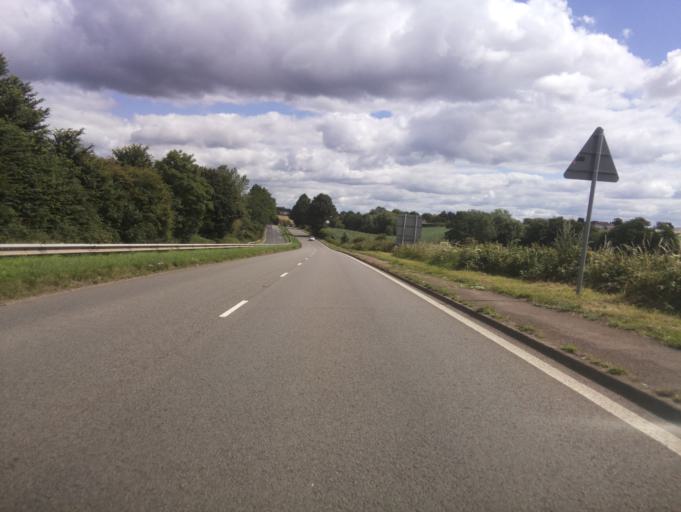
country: GB
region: England
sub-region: Gloucestershire
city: Bream
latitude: 51.6915
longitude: -2.5934
